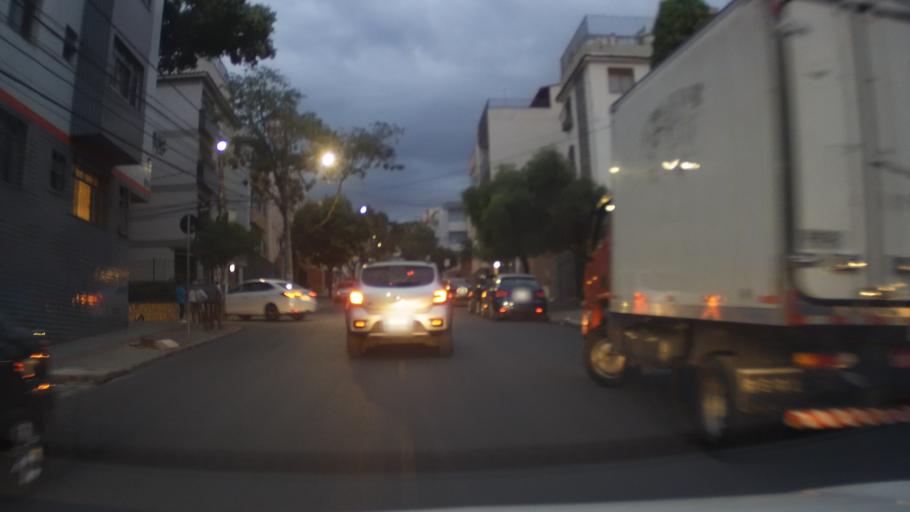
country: BR
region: Minas Gerais
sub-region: Belo Horizonte
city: Belo Horizonte
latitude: -19.8914
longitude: -43.9274
